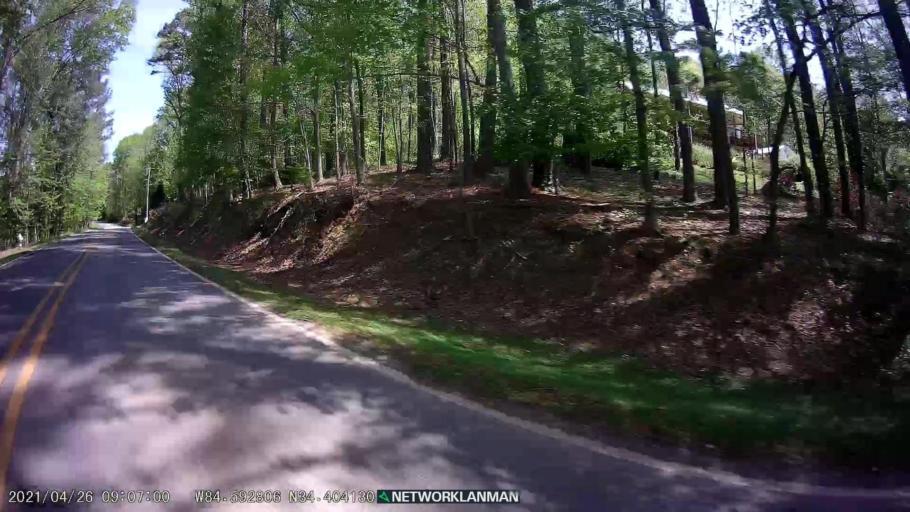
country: US
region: Georgia
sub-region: Bartow County
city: Rydal
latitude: 34.4047
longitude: -84.5925
